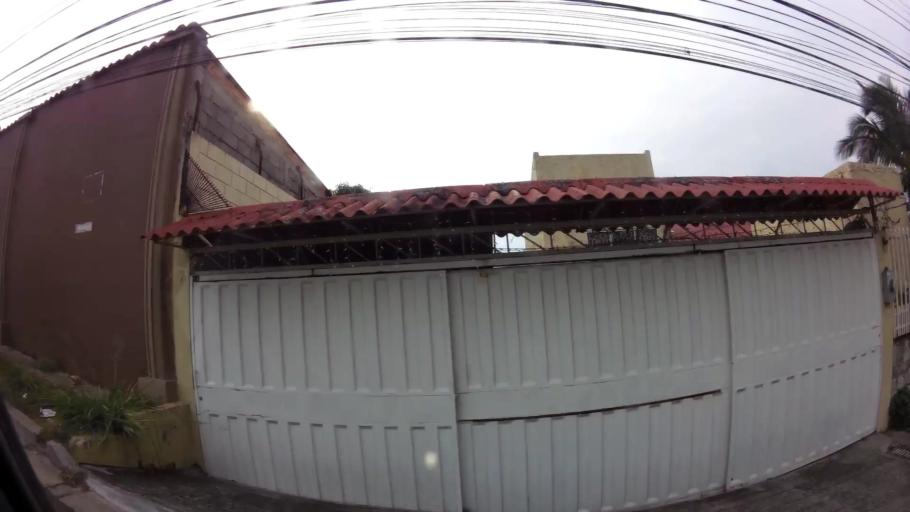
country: HN
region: Francisco Morazan
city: Tegucigalpa
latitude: 14.0815
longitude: -87.1975
